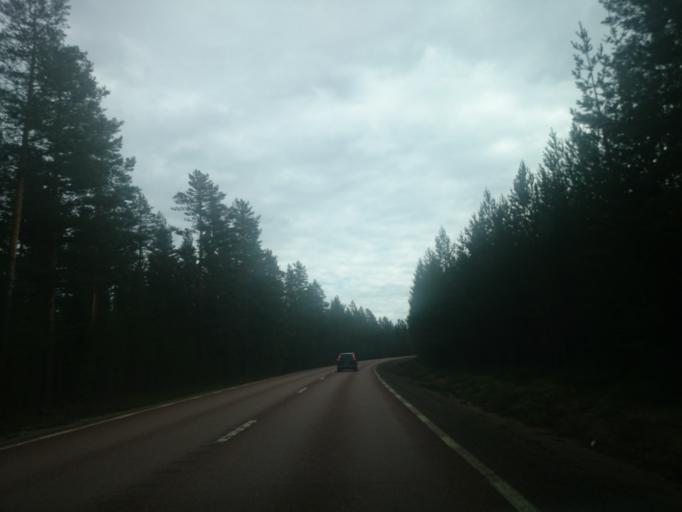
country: SE
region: Gaevleborg
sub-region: Ljusdals Kommun
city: Farila
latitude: 61.9164
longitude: 15.6206
